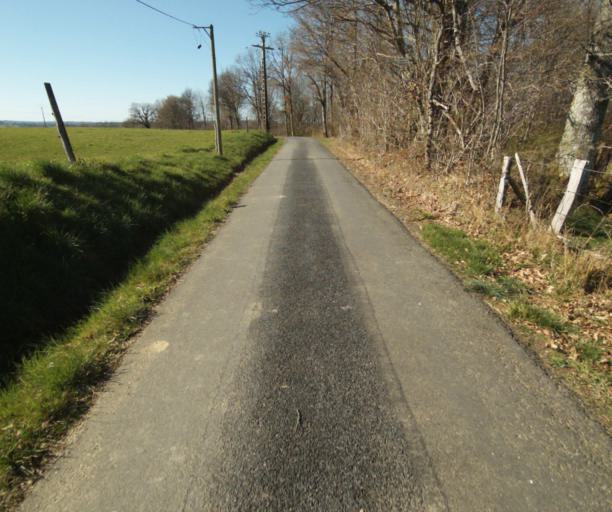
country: FR
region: Limousin
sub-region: Departement de la Correze
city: Chamboulive
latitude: 45.4368
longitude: 1.6701
